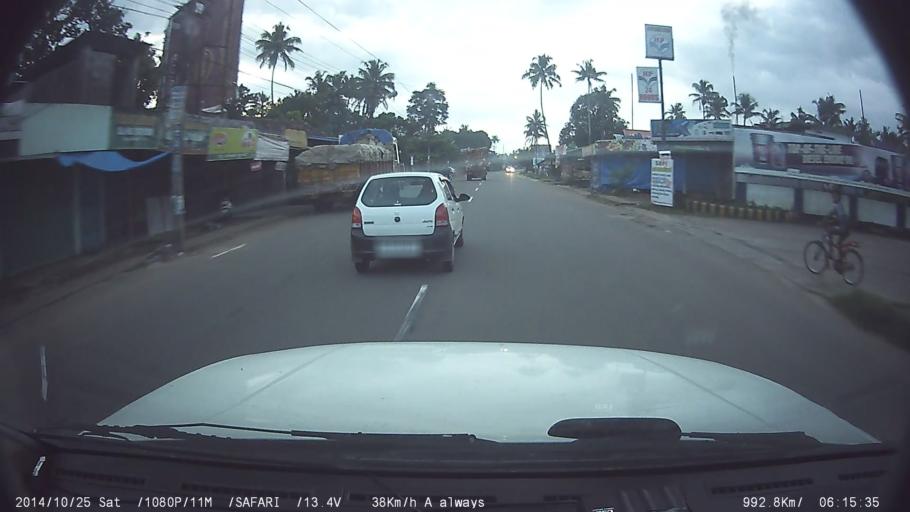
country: IN
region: Kerala
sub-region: Ernakulam
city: Perumpavur
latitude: 10.1311
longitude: 76.4704
